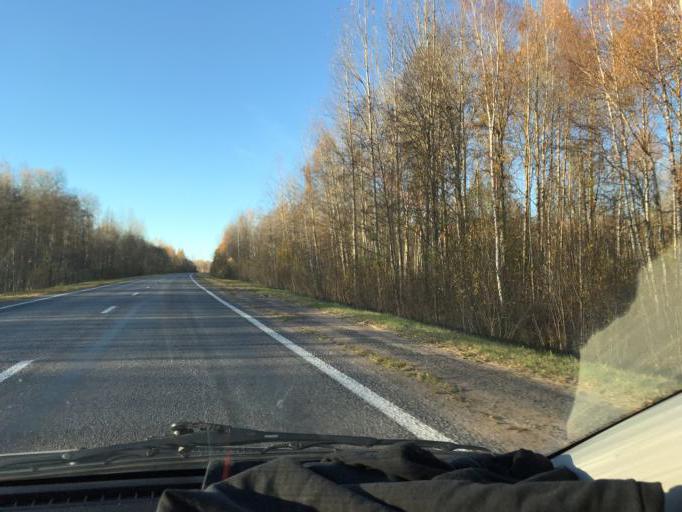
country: BY
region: Vitebsk
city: Vitebsk
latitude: 55.3657
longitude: 30.1605
